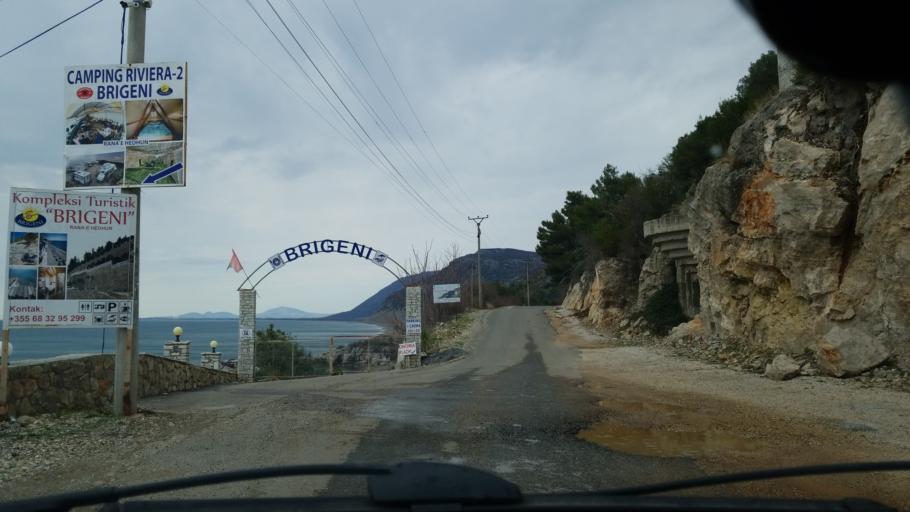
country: AL
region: Lezhe
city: Shengjin
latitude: 41.8150
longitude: 19.5696
